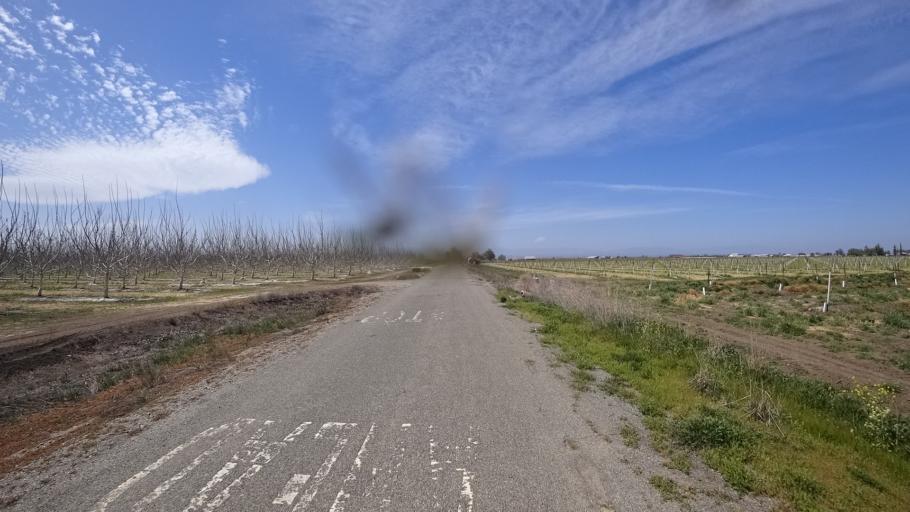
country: US
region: California
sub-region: Glenn County
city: Willows
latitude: 39.5678
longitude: -122.1957
